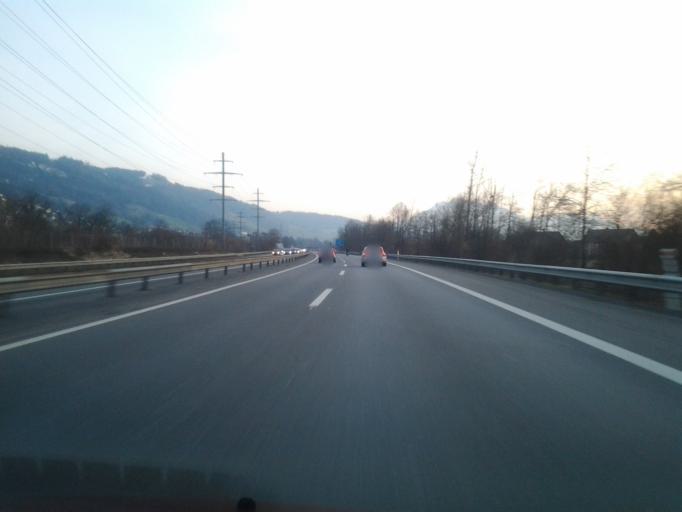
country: CH
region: Lucerne
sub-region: Lucerne-Land District
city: Root
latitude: 47.1337
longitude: 8.3989
